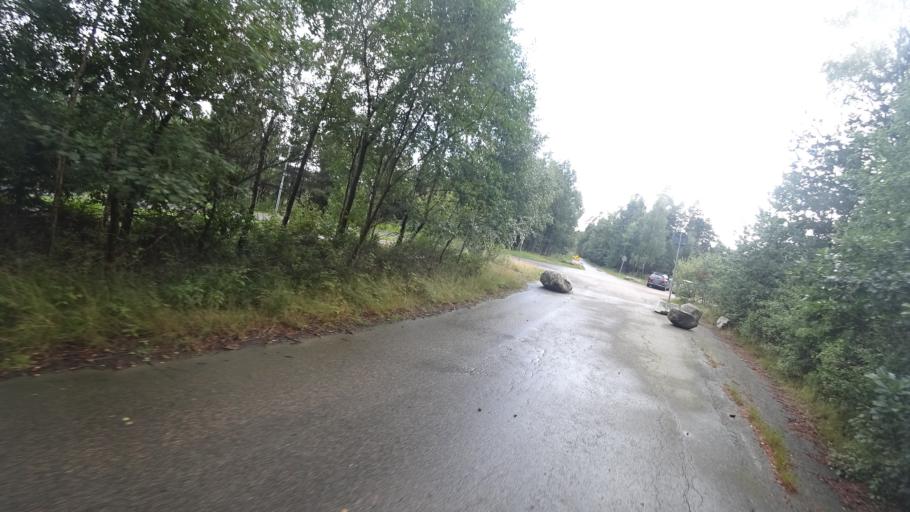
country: SE
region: Vaestra Goetaland
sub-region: Partille Kommun
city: Ojersjo
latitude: 57.6809
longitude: 12.0882
